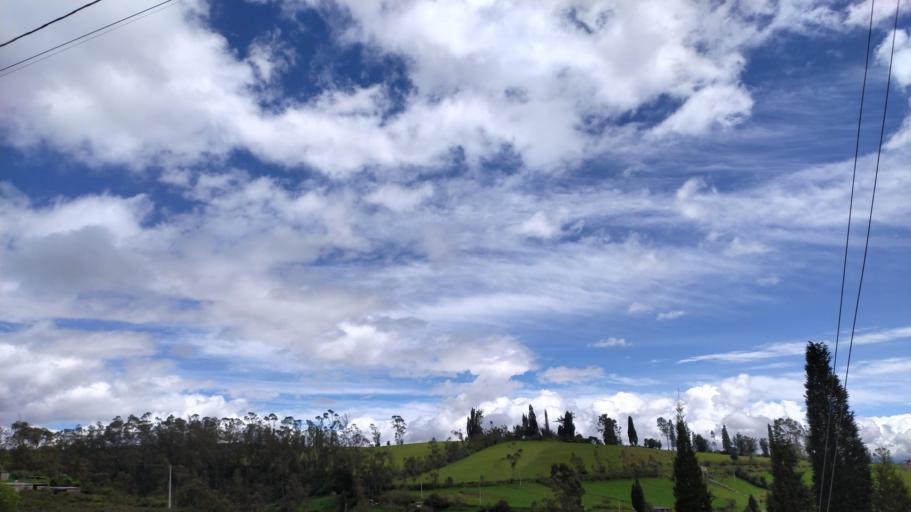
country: EC
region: Chimborazo
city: Riobamba
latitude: -1.6902
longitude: -78.5777
